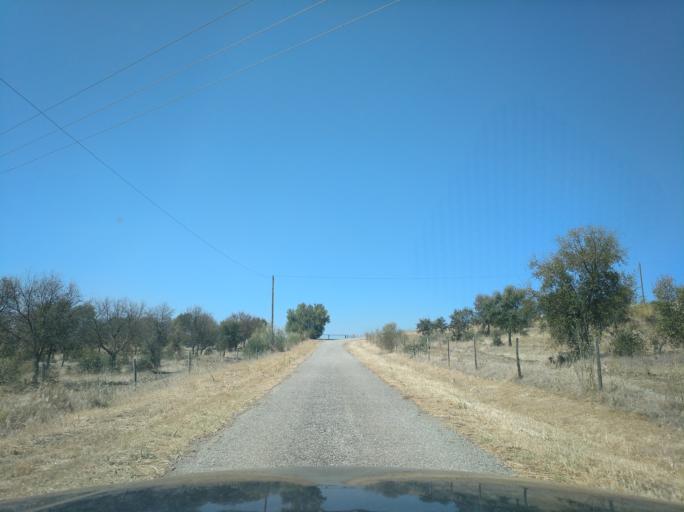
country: PT
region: Portalegre
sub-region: Campo Maior
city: Campo Maior
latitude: 39.0018
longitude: -7.0920
